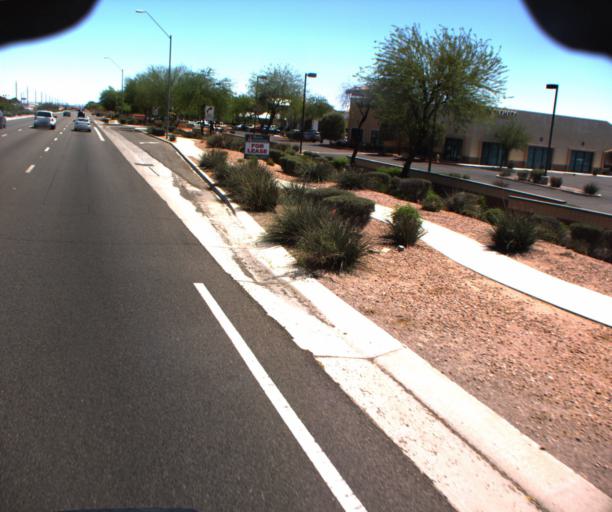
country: US
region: Arizona
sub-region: Maricopa County
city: Sun City West
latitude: 33.6535
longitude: -112.3695
